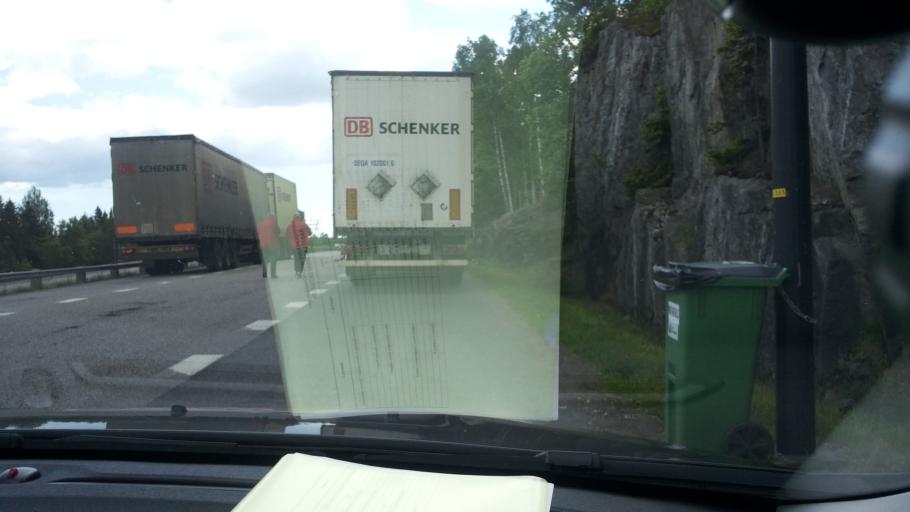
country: SE
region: Vaesternorrland
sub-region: Sundsvalls Kommun
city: Sundsbruk
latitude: 62.4605
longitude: 17.3396
